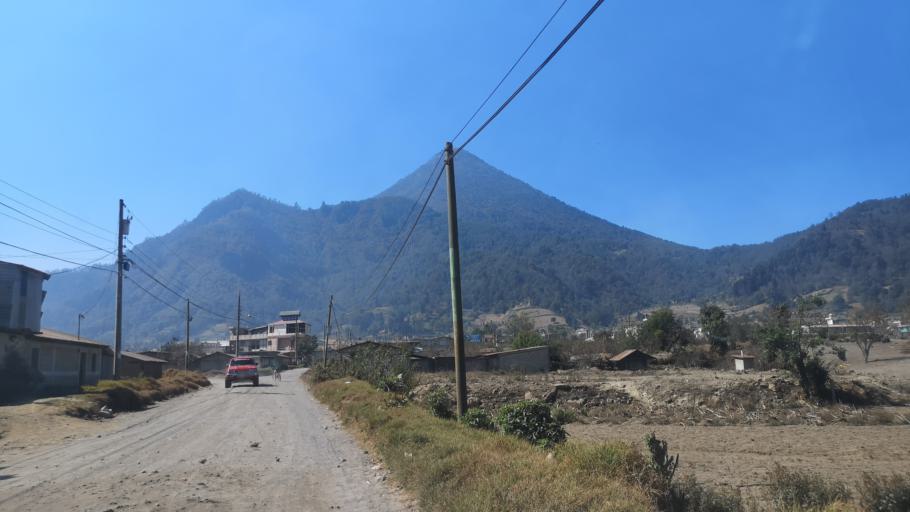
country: GT
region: Quetzaltenango
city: Quetzaltenango
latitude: 14.7935
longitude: -91.5436
